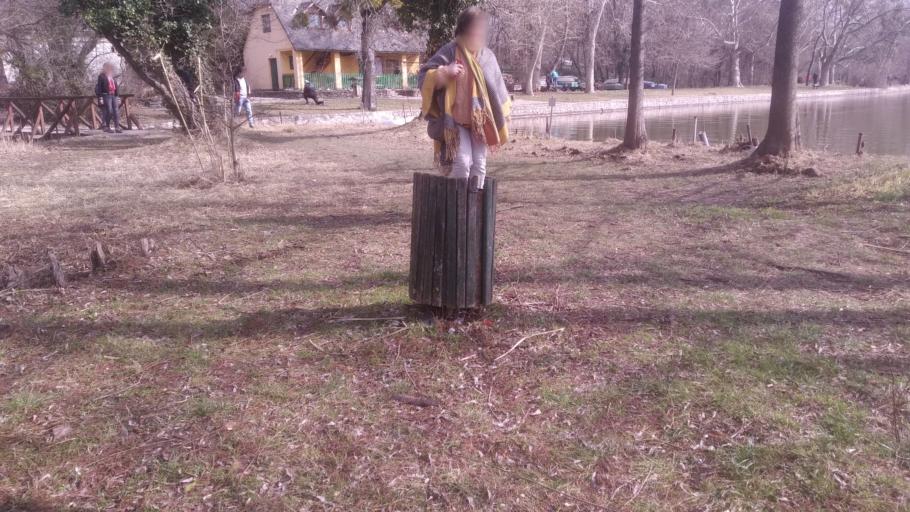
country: HU
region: Komarom-Esztergom
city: Tata
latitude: 47.6530
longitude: 18.3329
